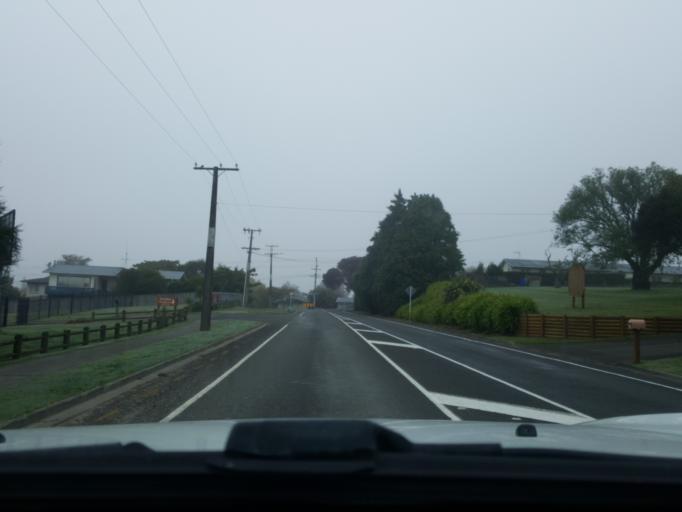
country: NZ
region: Waikato
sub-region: Hamilton City
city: Hamilton
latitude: -37.7683
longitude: 175.2308
